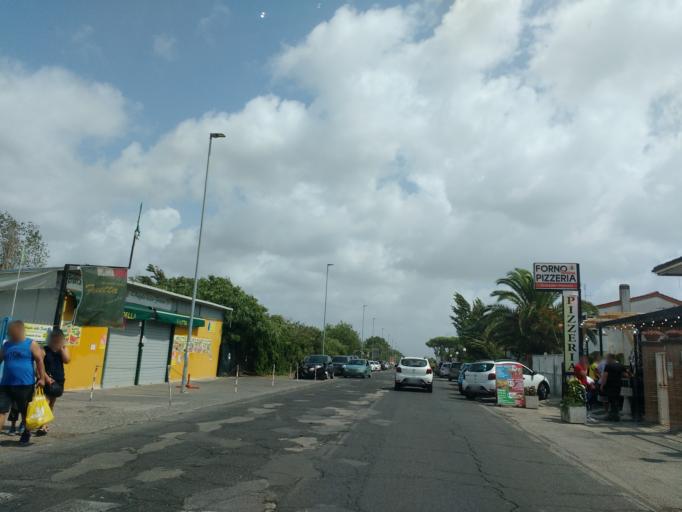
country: IT
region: Latium
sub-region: Citta metropolitana di Roma Capitale
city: Marina di Ardea-Tor San Lorenzo
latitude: 41.5633
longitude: 12.5280
